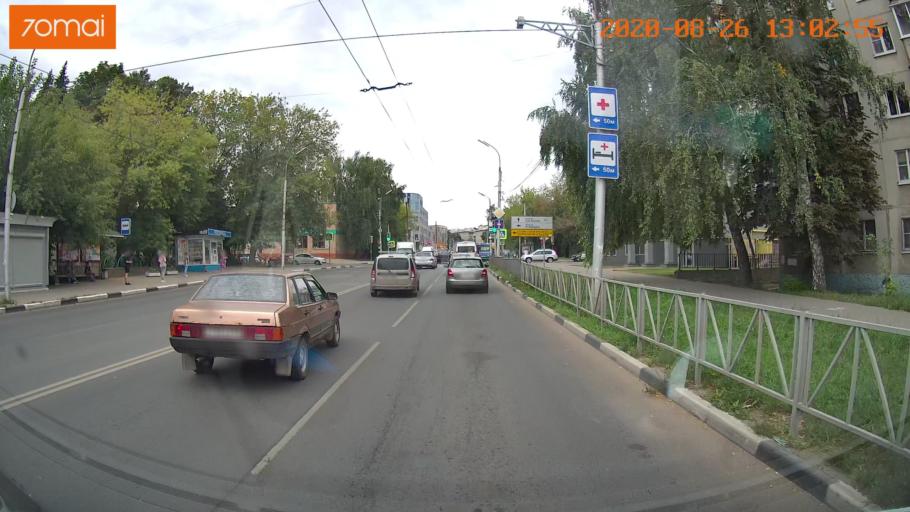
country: RU
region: Rjazan
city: Ryazan'
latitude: 54.6183
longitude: 39.7342
